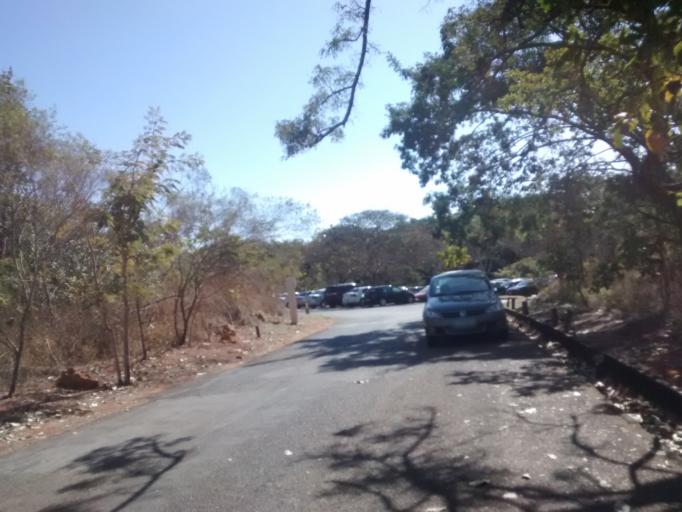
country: BR
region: Federal District
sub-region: Brasilia
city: Brasilia
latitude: -15.7400
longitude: -47.9251
